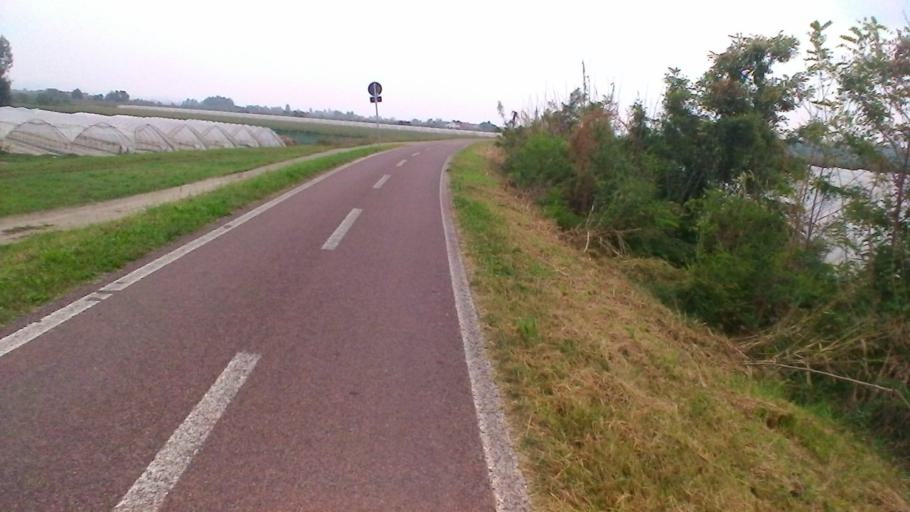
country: IT
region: Veneto
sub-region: Provincia di Verona
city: San Martino Buon Albergo
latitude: 45.3871
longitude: 11.0876
